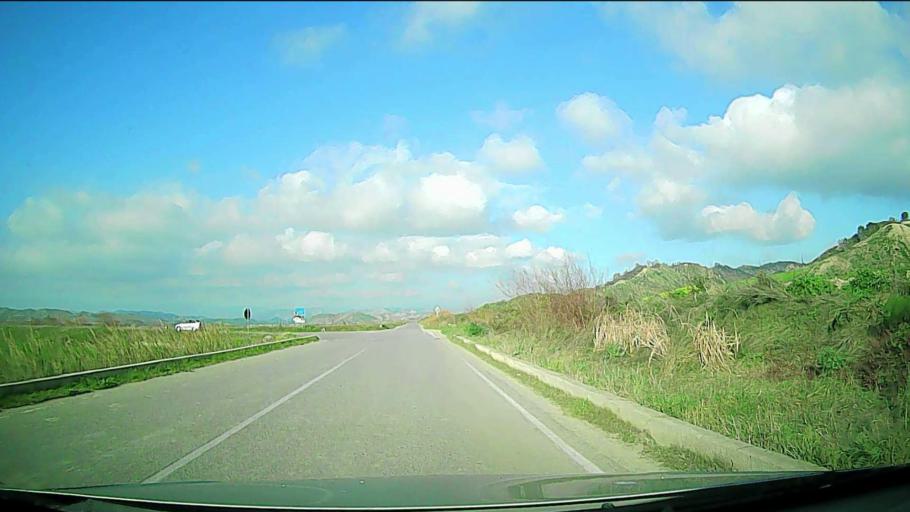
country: IT
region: Calabria
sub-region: Provincia di Crotone
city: Tronca
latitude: 39.2029
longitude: 17.0697
